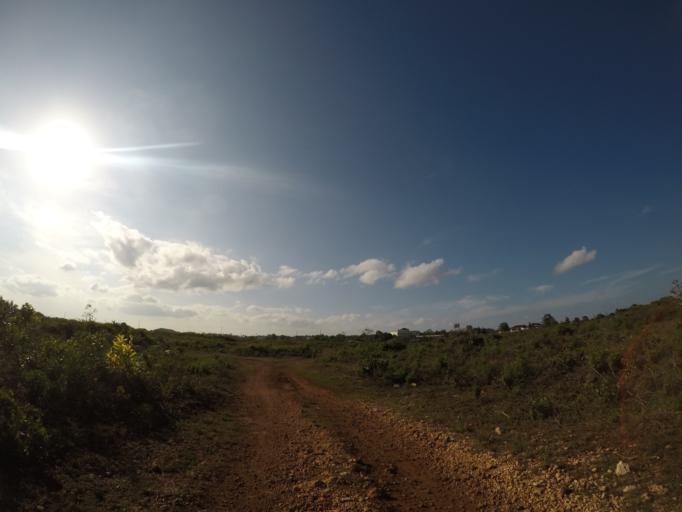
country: TZ
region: Zanzibar Central/South
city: Koani
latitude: -6.2029
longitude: 39.3098
